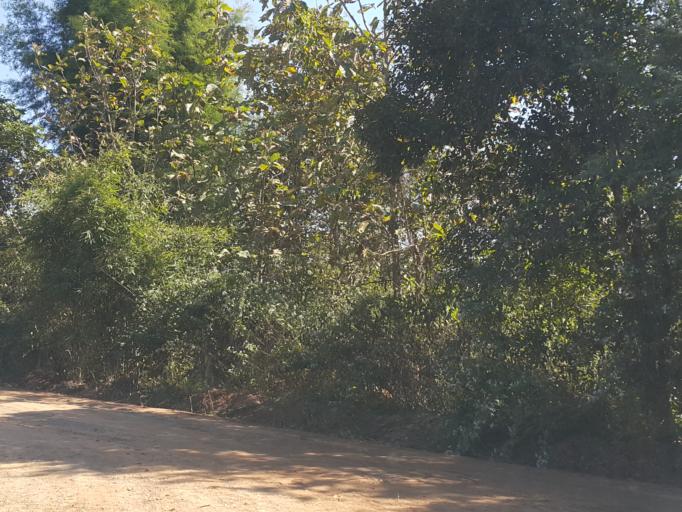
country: TH
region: Chiang Mai
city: Mae Taeng
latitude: 18.9511
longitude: 98.9042
